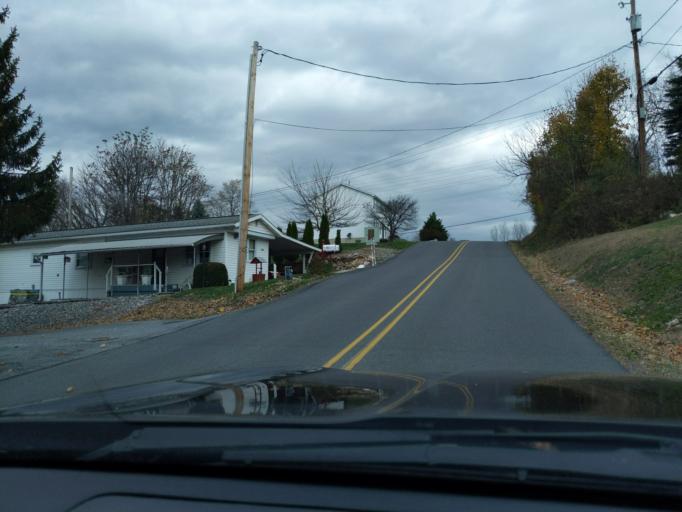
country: US
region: Pennsylvania
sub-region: Blair County
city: Greenwood
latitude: 40.5333
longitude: -78.3670
